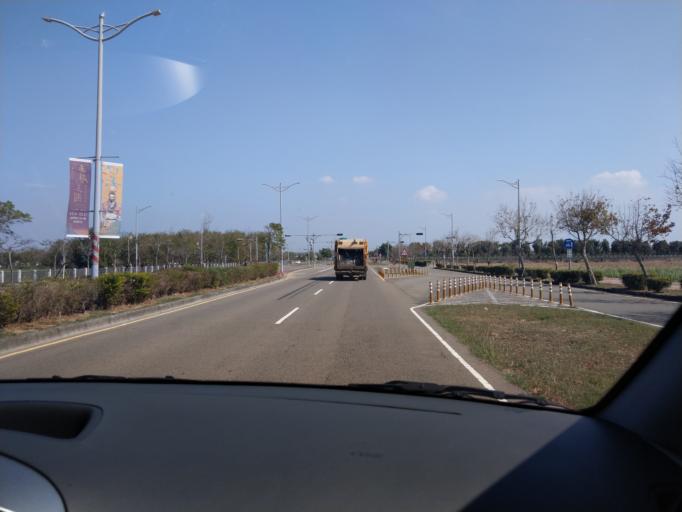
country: TW
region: Taiwan
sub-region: Chiayi
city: Taibao
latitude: 23.4664
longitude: 120.3158
